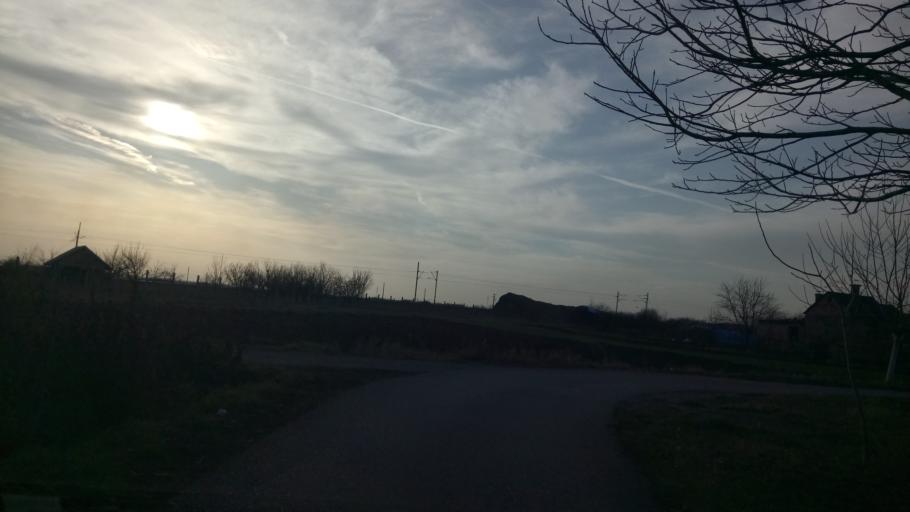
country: RS
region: Autonomna Pokrajina Vojvodina
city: Nova Pazova
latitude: 44.9321
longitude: 20.2215
